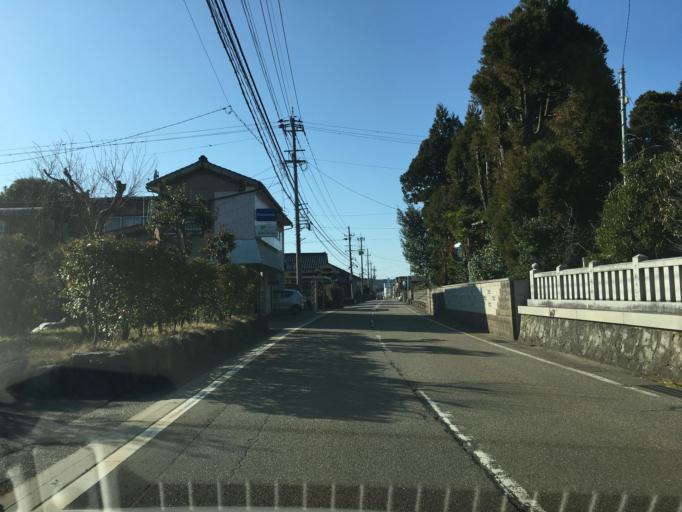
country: JP
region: Toyama
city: Himi
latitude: 36.8325
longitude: 136.9959
